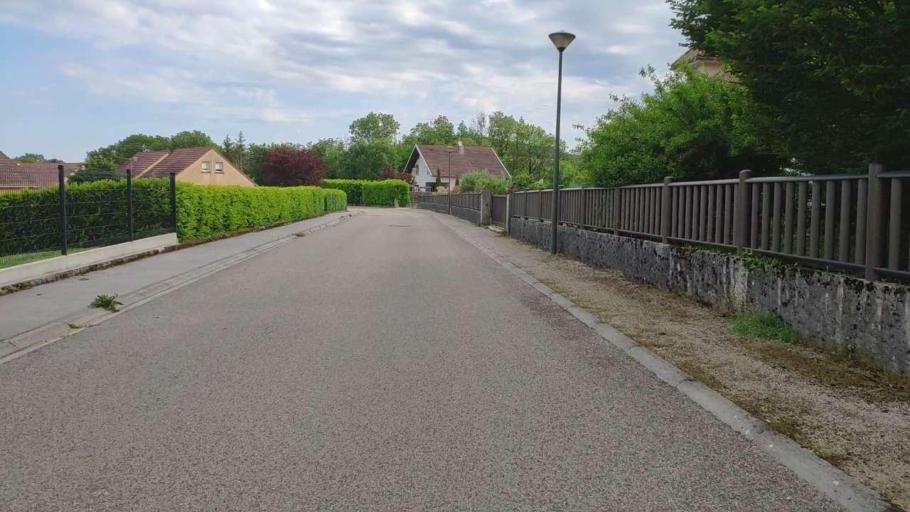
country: FR
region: Franche-Comte
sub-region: Departement du Jura
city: Perrigny
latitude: 46.7594
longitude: 5.6037
